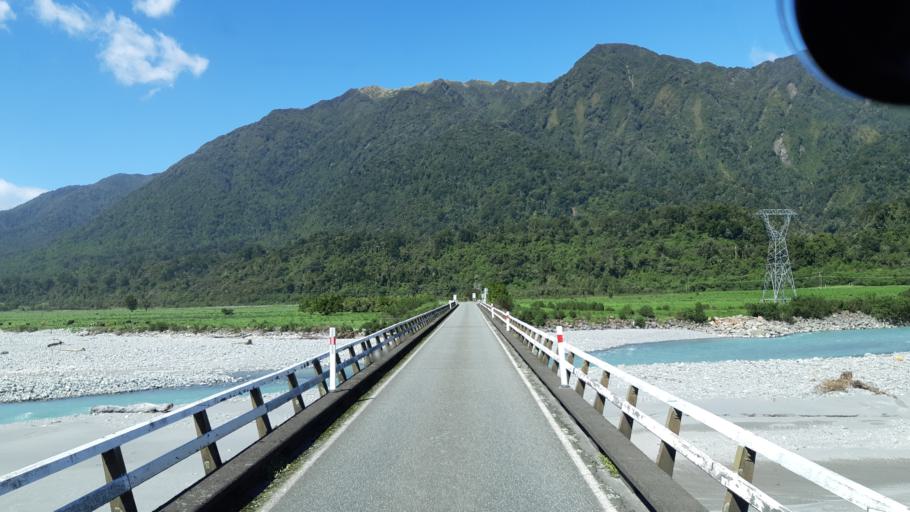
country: NZ
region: West Coast
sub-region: Westland District
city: Hokitika
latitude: -43.1555
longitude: 170.6234
